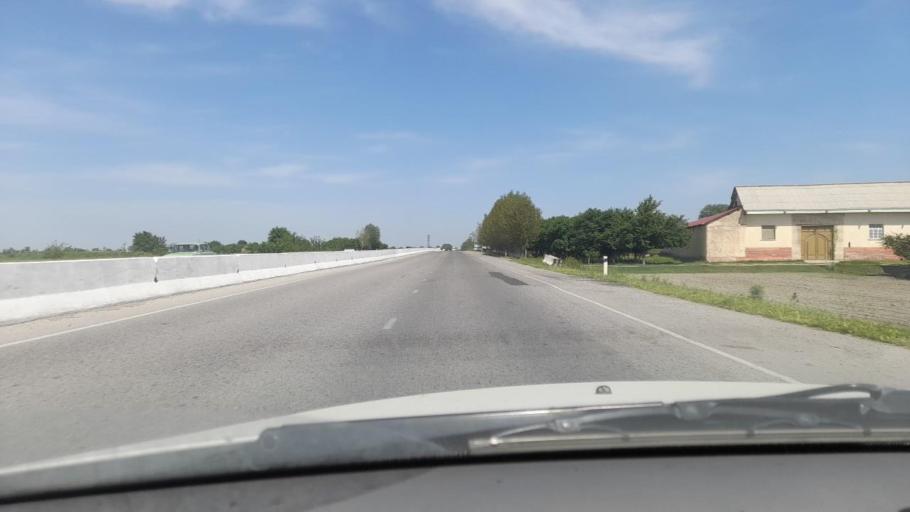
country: UZ
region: Samarqand
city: Kattaqo'rg'on
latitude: 39.9195
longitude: 66.3400
